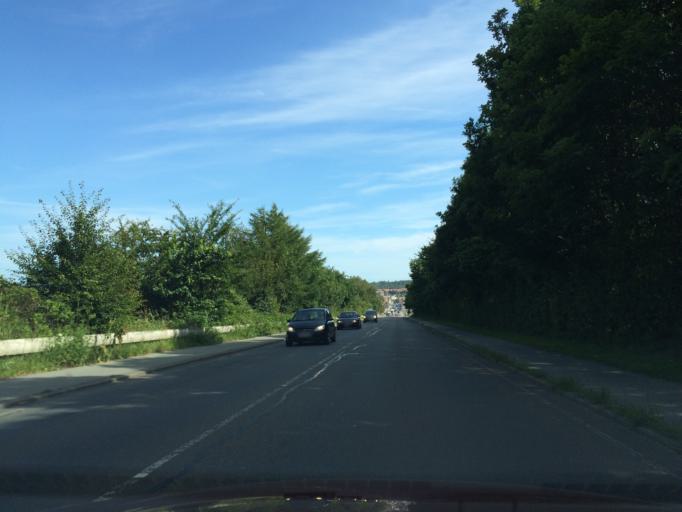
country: DK
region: Central Jutland
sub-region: Silkeborg Kommune
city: Silkeborg
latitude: 56.1885
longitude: 9.5390
